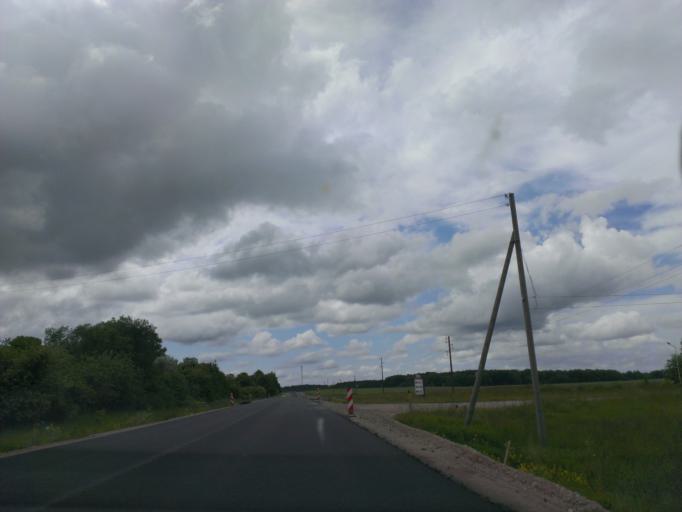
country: LV
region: Durbe
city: Liegi
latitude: 56.5895
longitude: 21.4204
